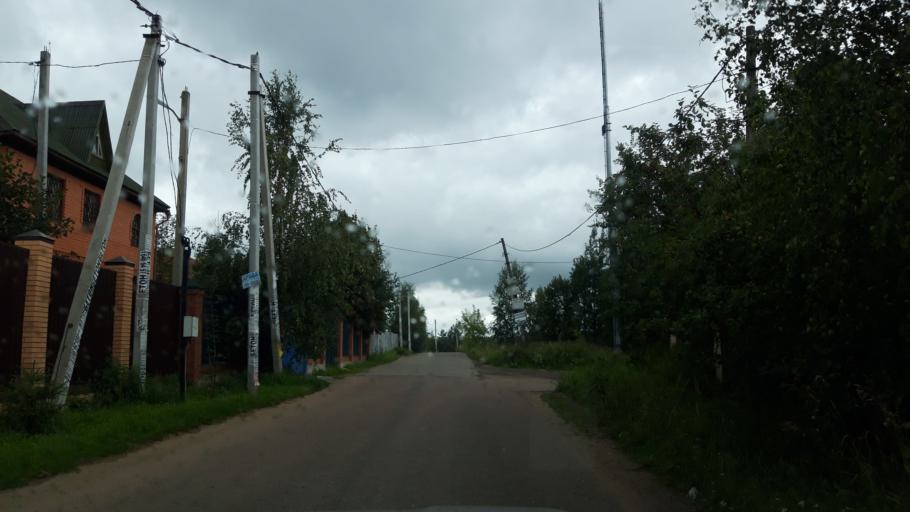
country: RU
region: Moskovskaya
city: Povarovo
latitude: 56.0944
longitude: 37.0727
